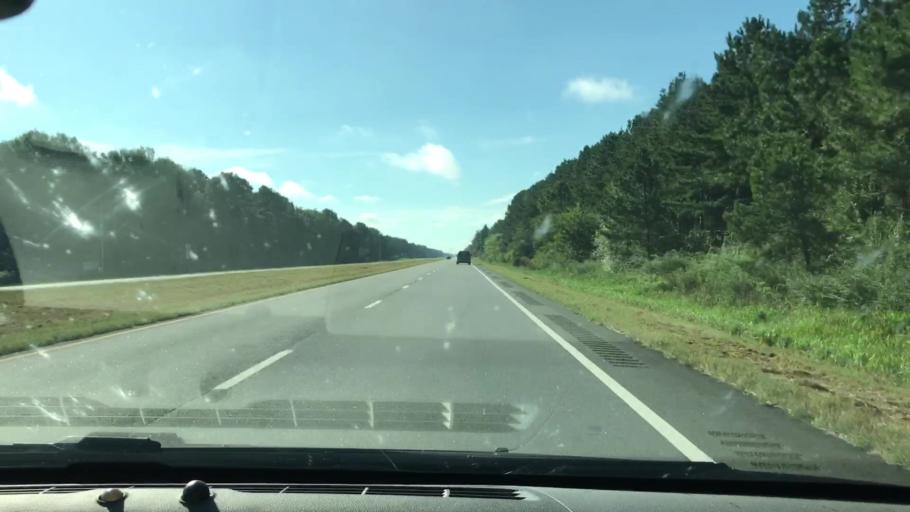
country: US
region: Georgia
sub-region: Lee County
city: Leesburg
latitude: 31.6947
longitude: -84.3172
